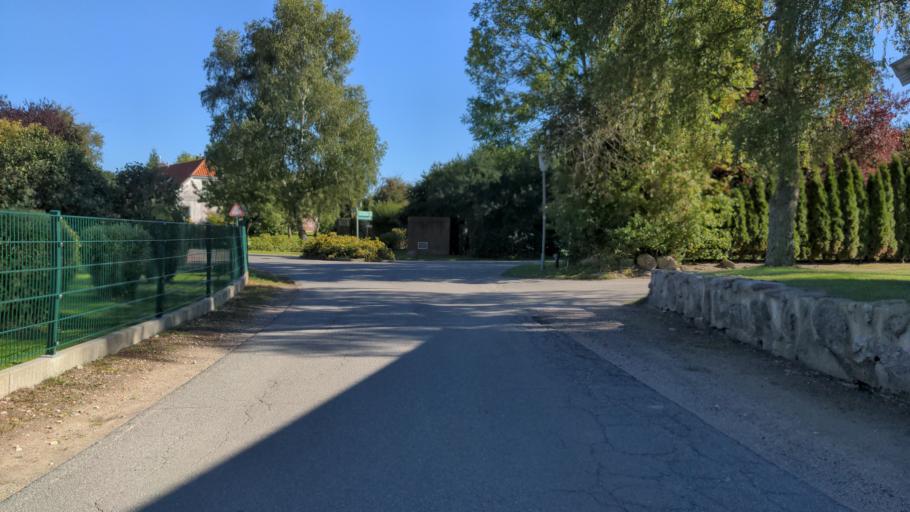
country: DE
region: Schleswig-Holstein
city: Manhagen
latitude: 54.1645
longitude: 10.9274
